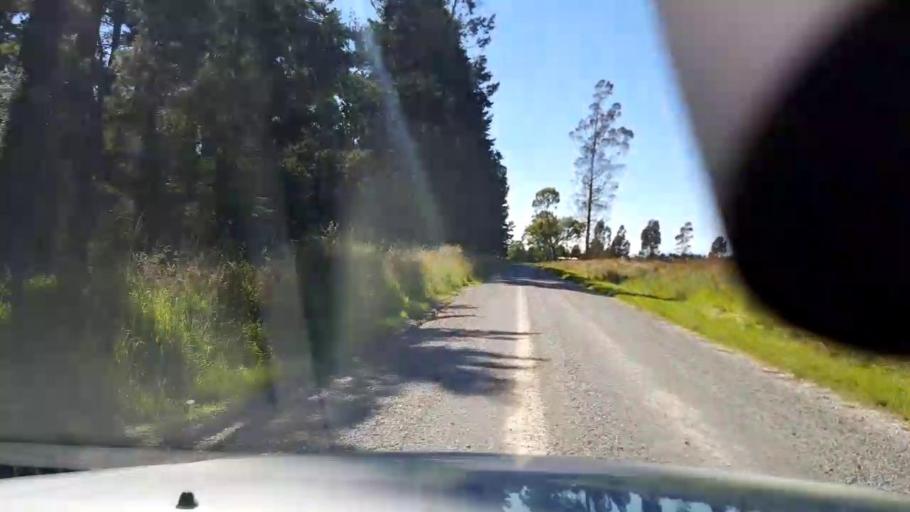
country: NZ
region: Canterbury
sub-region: Timaru District
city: Pleasant Point
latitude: -43.9785
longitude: 171.2758
